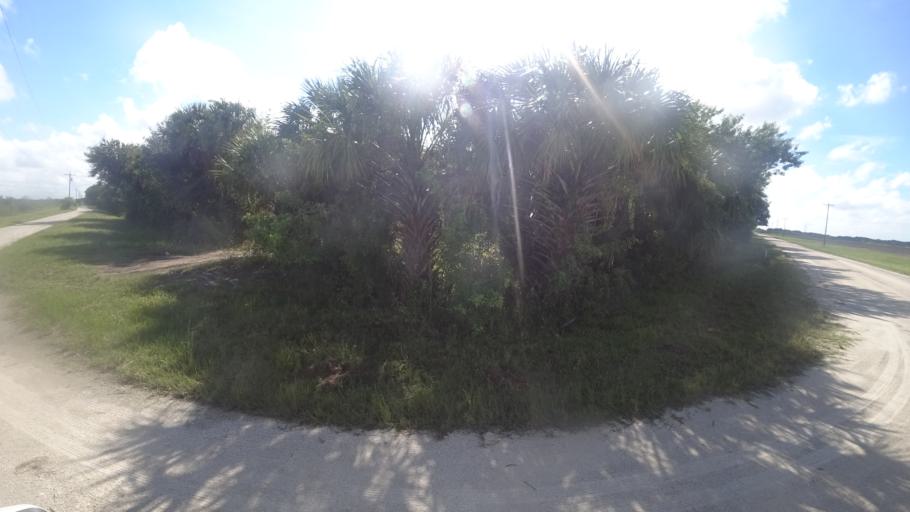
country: US
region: Florida
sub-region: Hillsborough County
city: Ruskin
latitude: 27.6307
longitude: -82.4970
